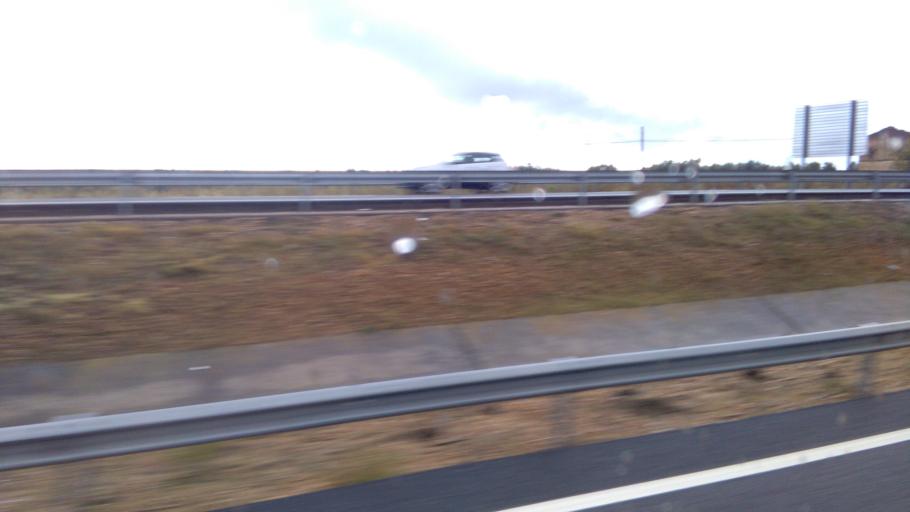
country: ES
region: Castille-La Mancha
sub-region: Province of Toledo
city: Cazalegas
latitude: 39.9953
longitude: -4.6791
